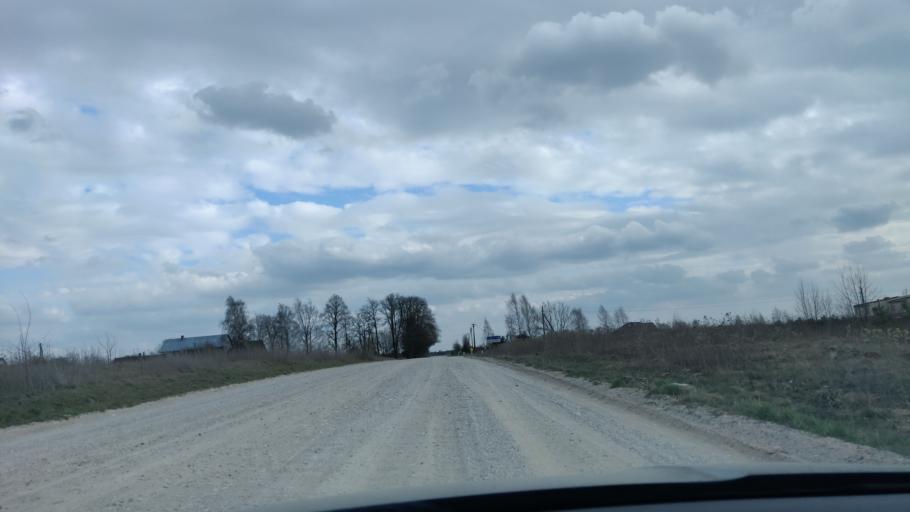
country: LT
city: Lentvaris
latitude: 54.6173
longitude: 25.0674
